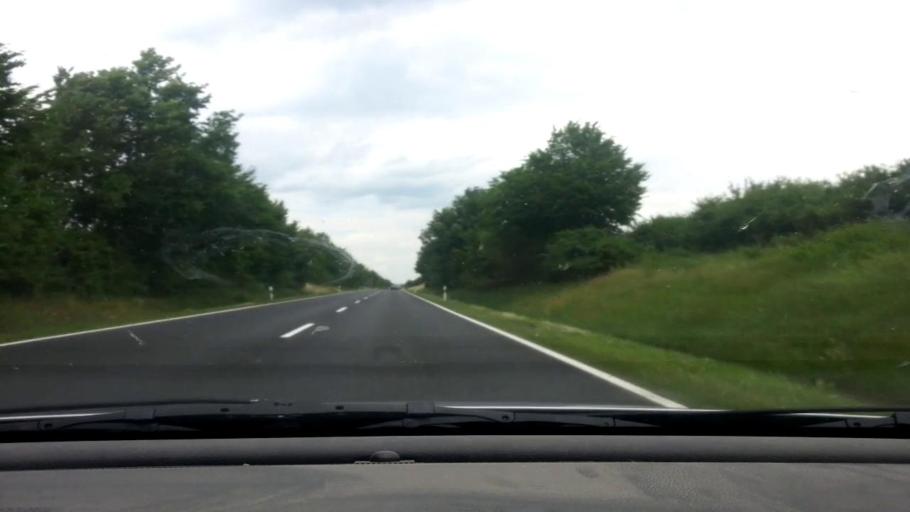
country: DE
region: Bavaria
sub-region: Upper Palatinate
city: Waldsassen
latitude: 49.9832
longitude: 12.2768
